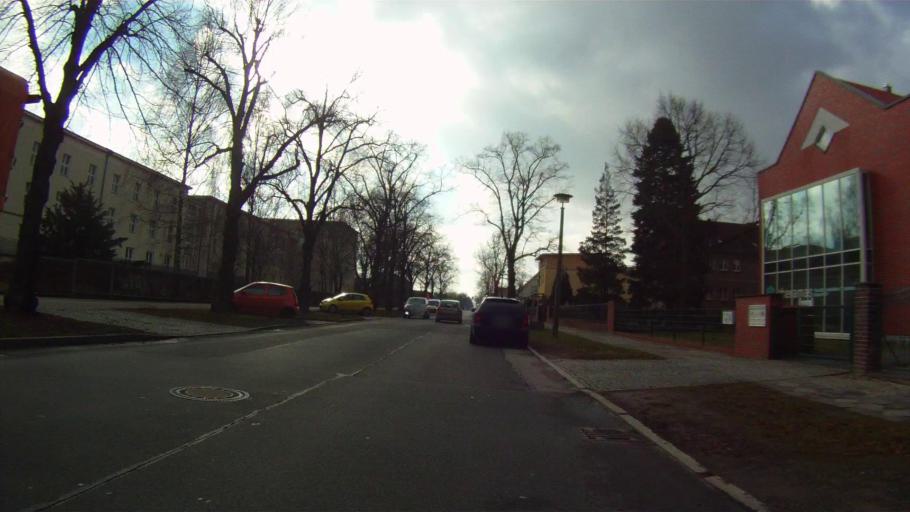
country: DE
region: Berlin
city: Biesdorf
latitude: 52.5269
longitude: 13.5574
